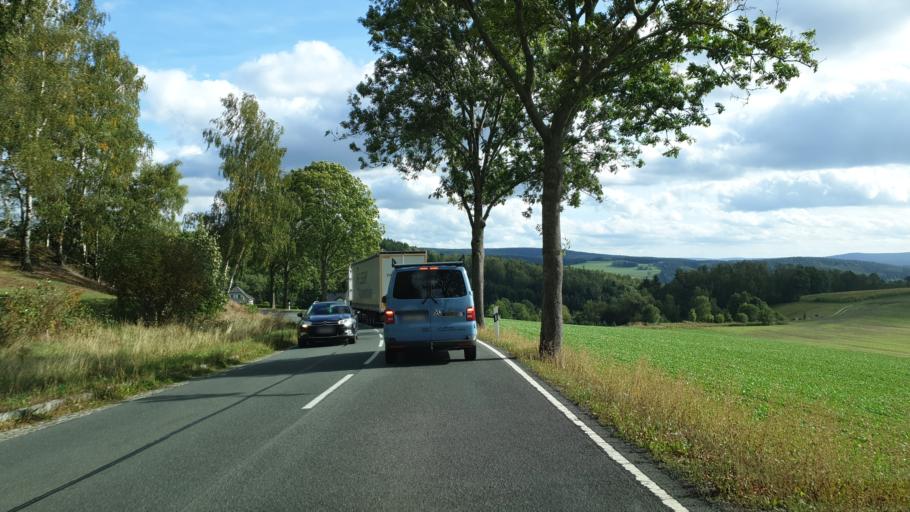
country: DE
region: Saxony
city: Lossnitz
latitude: 50.6421
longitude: 12.7320
